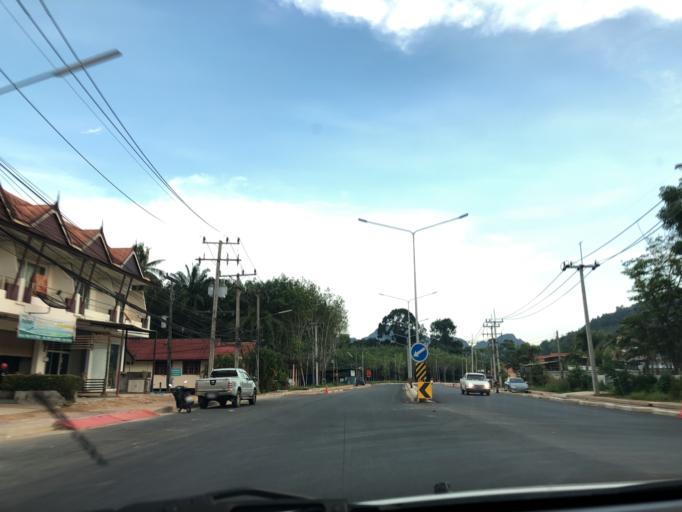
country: TH
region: Phangnga
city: Ban Ao Nang
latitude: 8.0592
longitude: 98.8404
